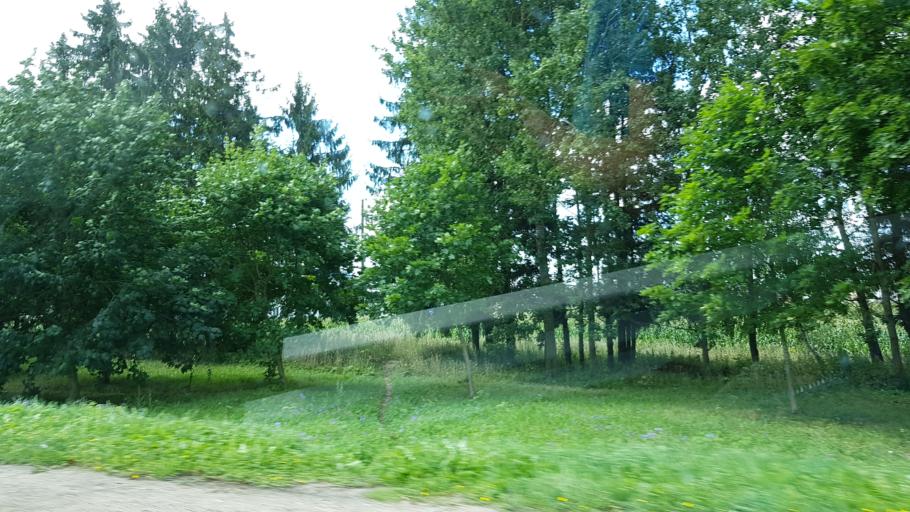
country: BY
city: Fanipol
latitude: 53.7349
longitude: 27.3290
